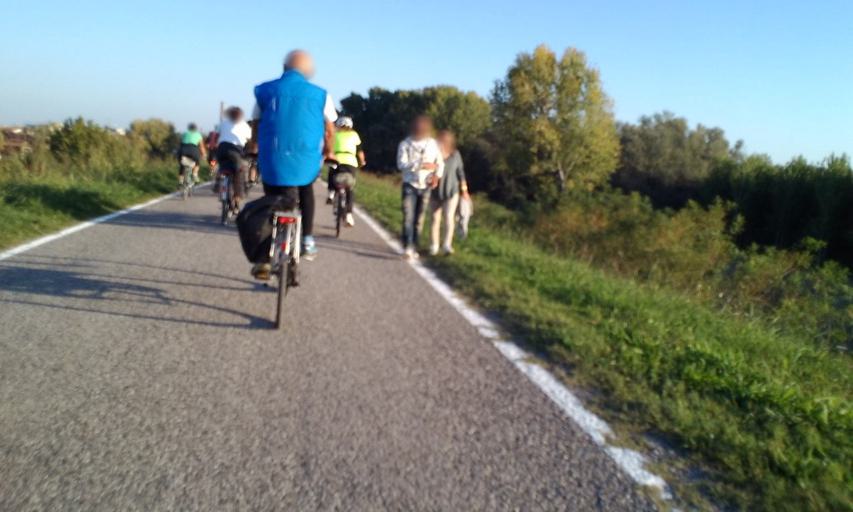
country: IT
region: Lombardy
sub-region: Provincia di Mantova
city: Ostiglia
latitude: 45.0734
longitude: 11.1232
